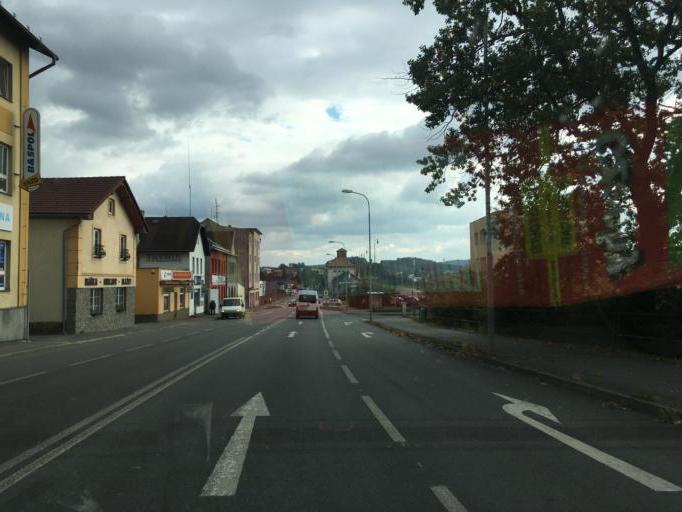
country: CZ
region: Vysocina
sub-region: Okres Pelhrimov
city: Pelhrimov
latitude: 49.4204
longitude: 15.2234
